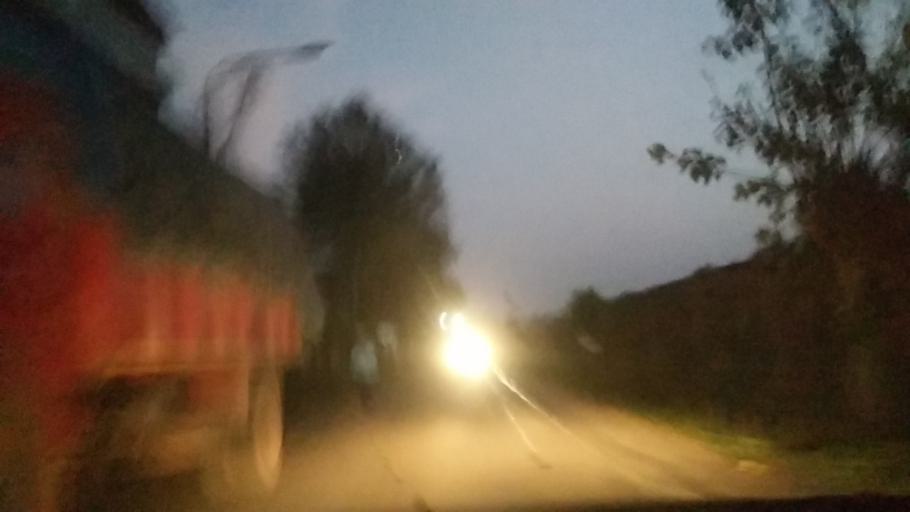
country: IN
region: Goa
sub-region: South Goa
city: Madgaon
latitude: 15.2674
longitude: 73.9647
